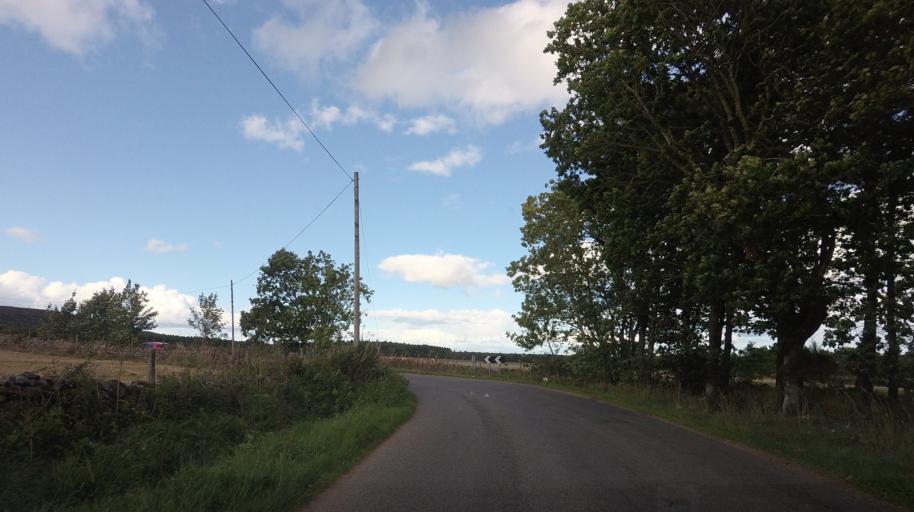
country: GB
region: Scotland
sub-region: Aberdeenshire
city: Banchory
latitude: 57.0940
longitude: -2.4479
